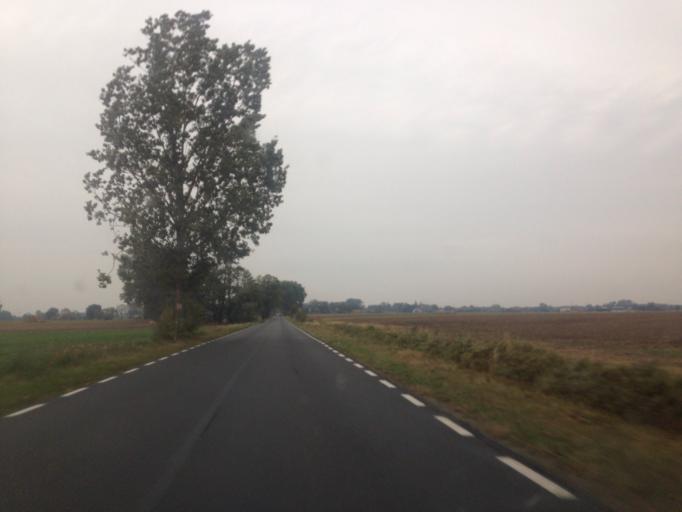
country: PL
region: Greater Poland Voivodeship
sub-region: Powiat poznanski
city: Swarzedz
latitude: 52.3476
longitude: 17.0968
